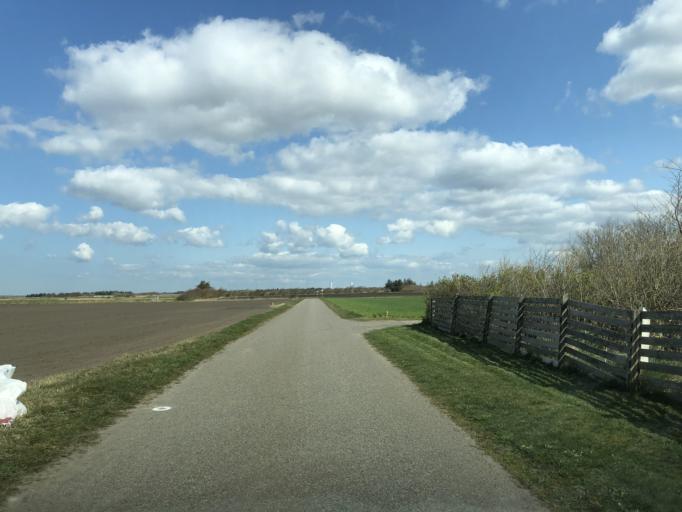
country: DK
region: Central Jutland
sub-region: Holstebro Kommune
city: Ulfborg
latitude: 56.4014
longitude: 8.1767
